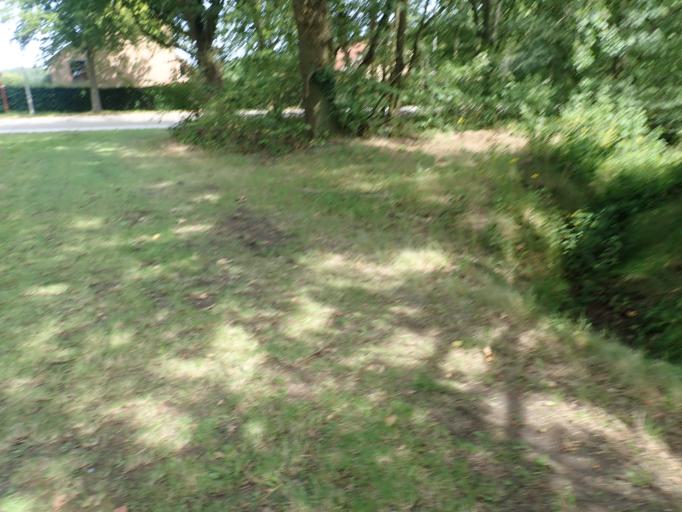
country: BE
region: Flanders
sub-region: Provincie Antwerpen
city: Zandhoven
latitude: 51.1992
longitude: 4.6649
